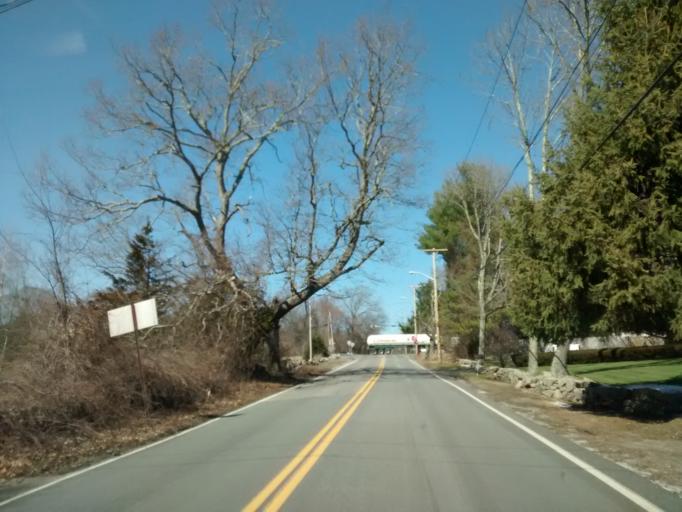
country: US
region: Massachusetts
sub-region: Worcester County
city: Northbridge
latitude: 42.1534
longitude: -71.6799
